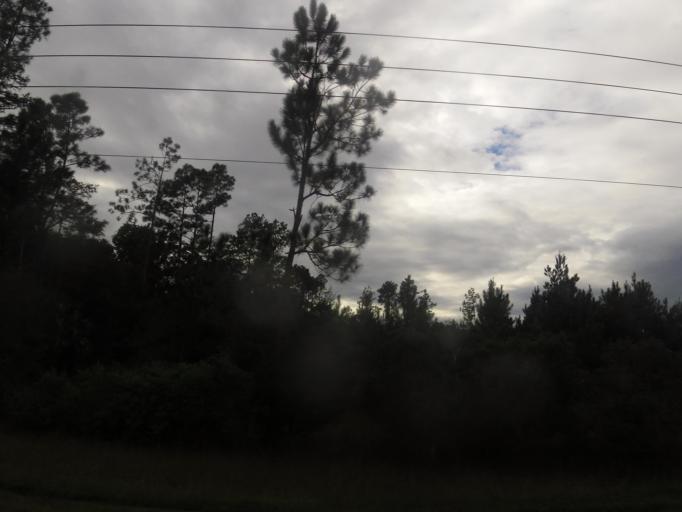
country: US
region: Florida
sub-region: Flagler County
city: Bunnell
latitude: 29.5005
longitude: -81.3475
